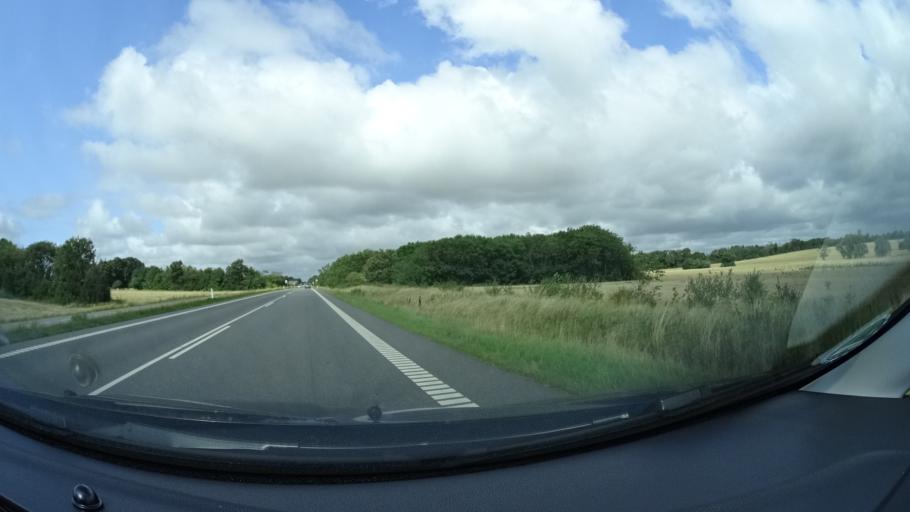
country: DK
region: Central Jutland
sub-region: Holstebro Kommune
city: Ulfborg
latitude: 56.2944
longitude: 8.3388
